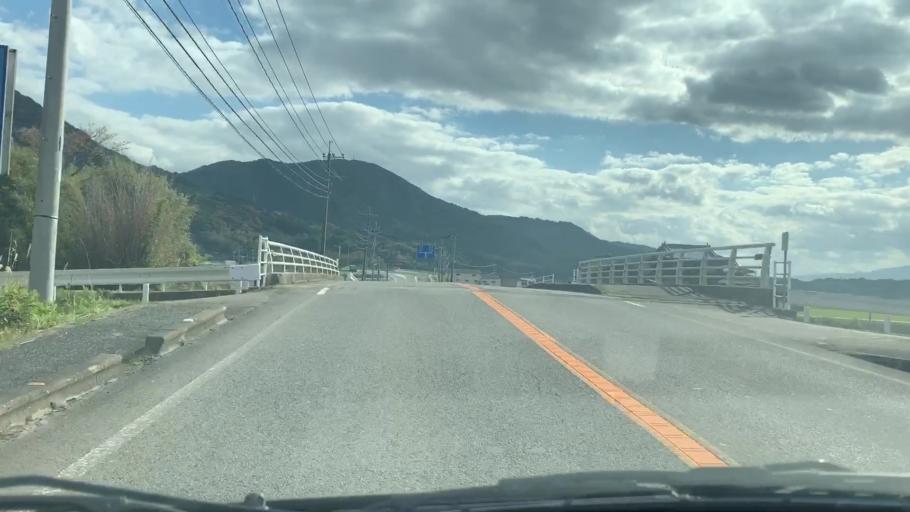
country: JP
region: Saga Prefecture
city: Takeocho-takeo
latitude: 33.2043
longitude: 130.0499
